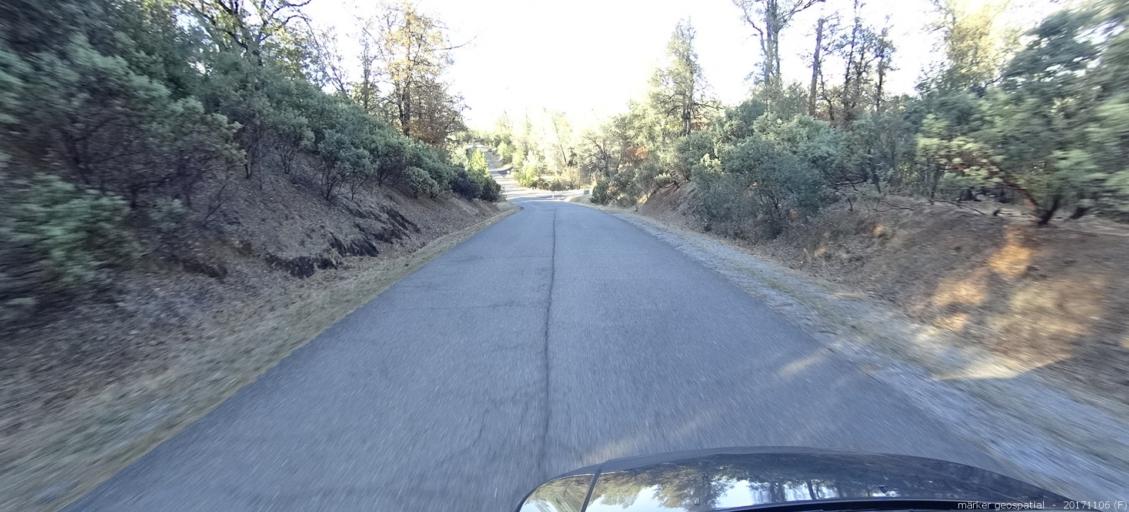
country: US
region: California
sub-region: Shasta County
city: Shasta
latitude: 40.5762
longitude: -122.4613
